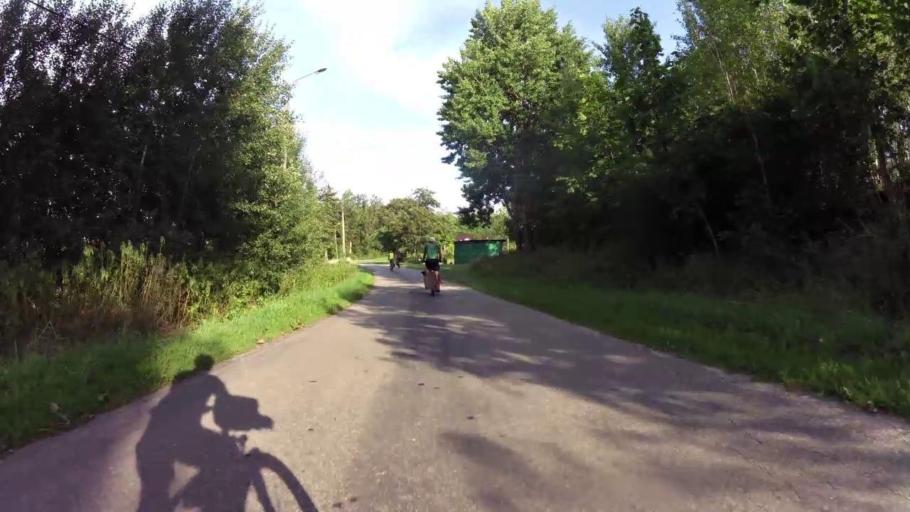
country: PL
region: West Pomeranian Voivodeship
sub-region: Powiat drawski
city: Drawsko Pomorskie
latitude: 53.4899
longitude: 15.7916
